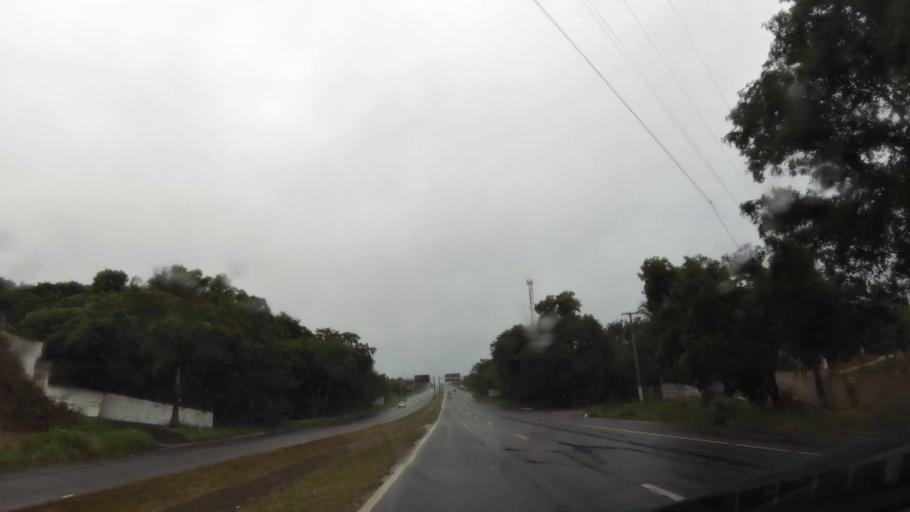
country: BR
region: Espirito Santo
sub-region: Viana
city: Viana
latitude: -20.5232
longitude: -40.3738
